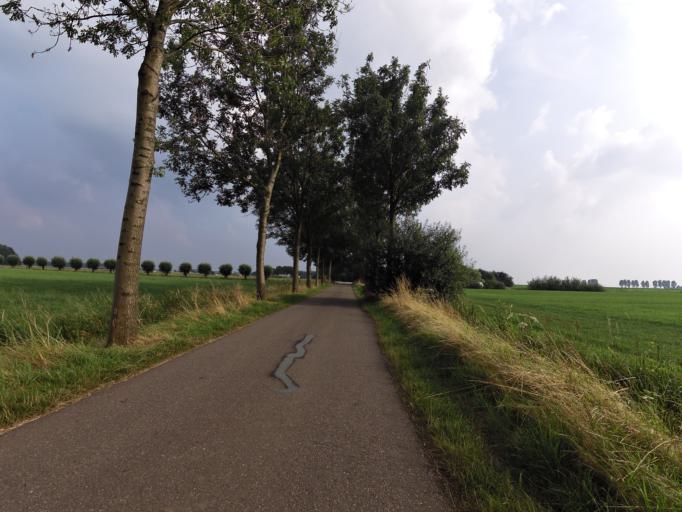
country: NL
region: Gelderland
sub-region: Gemeente Rheden
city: De Steeg
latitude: 51.9829
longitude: 6.0611
